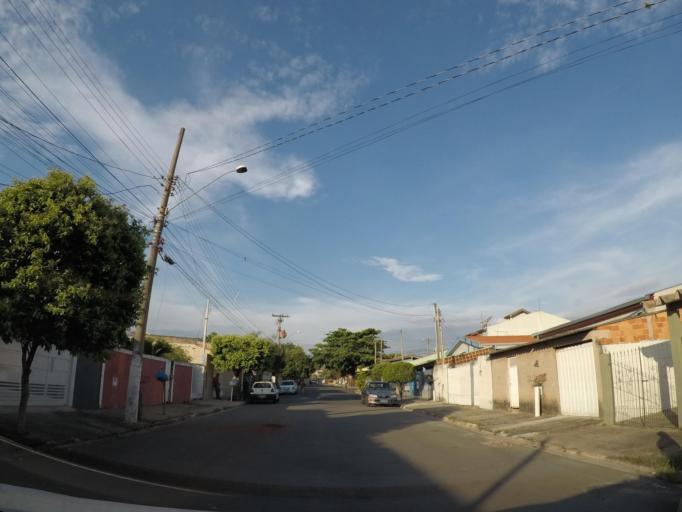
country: BR
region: Sao Paulo
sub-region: Sumare
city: Sumare
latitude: -22.8159
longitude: -47.2641
